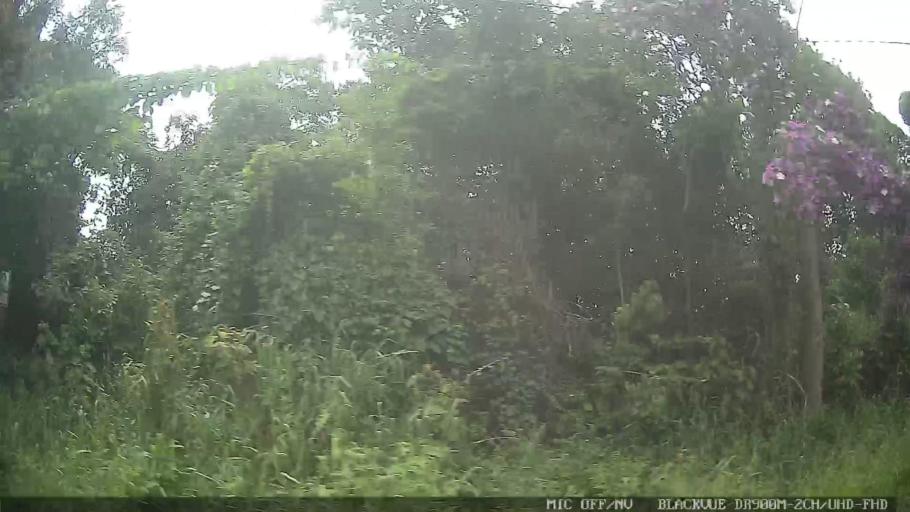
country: BR
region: Sao Paulo
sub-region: Suzano
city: Suzano
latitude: -23.4847
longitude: -46.2637
